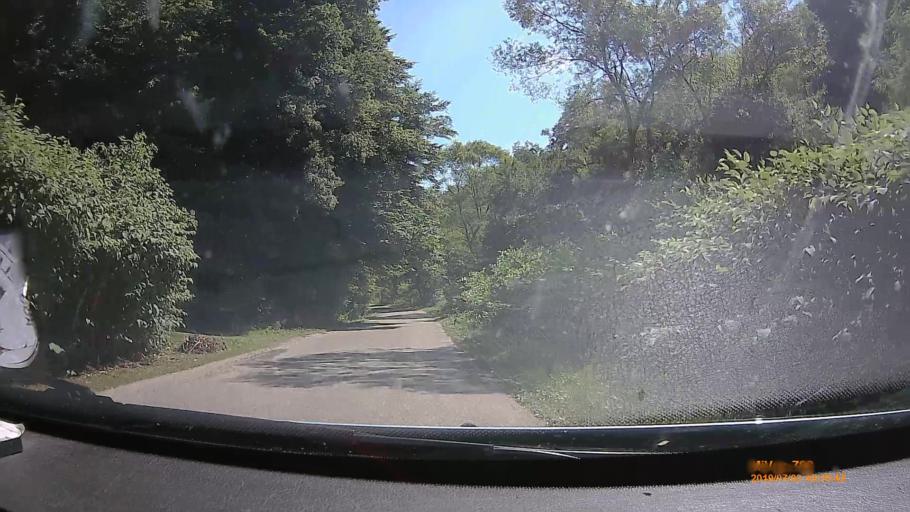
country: HU
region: Borsod-Abauj-Zemplen
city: Farkaslyuk
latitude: 48.2296
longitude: 20.3732
